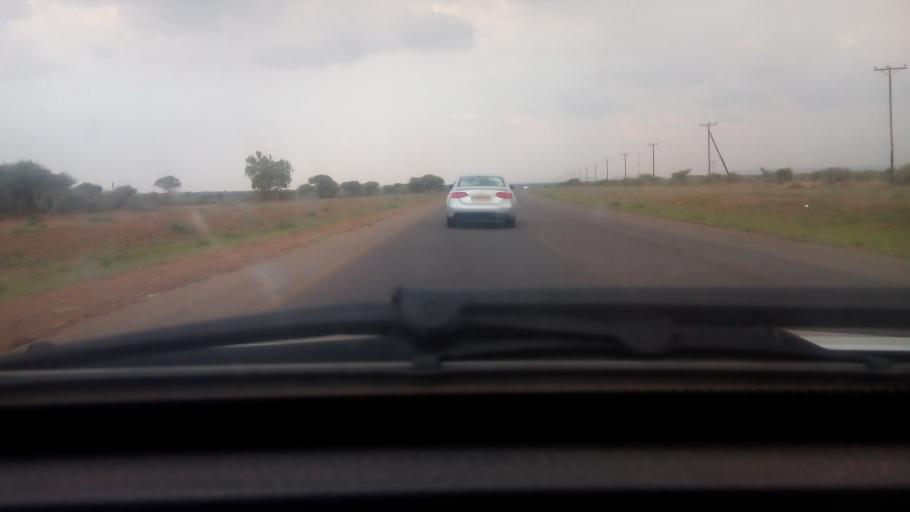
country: BW
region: Kweneng
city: Molepolole
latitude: -24.4558
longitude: 25.6517
